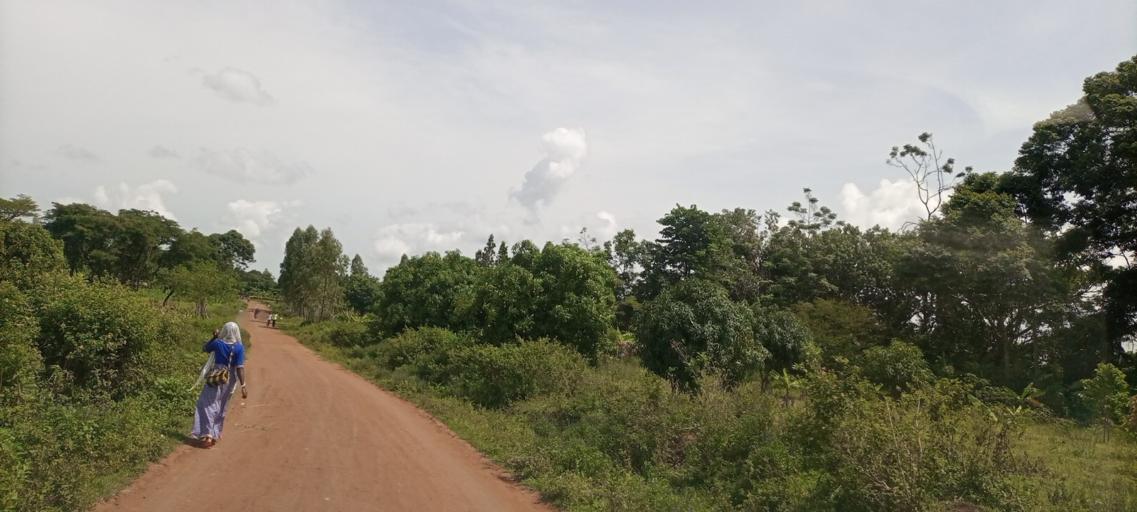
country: UG
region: Eastern Region
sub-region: Budaka District
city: Budaka
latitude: 1.1728
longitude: 33.9321
